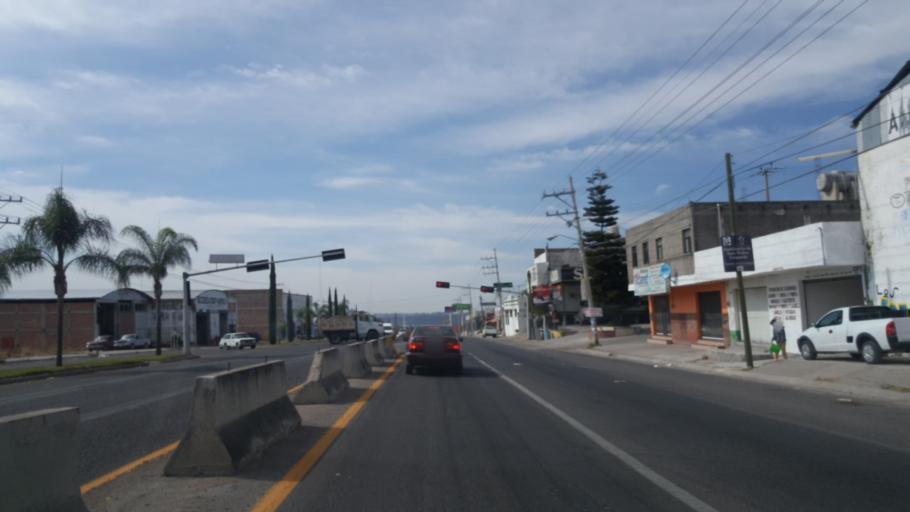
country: MX
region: Jalisco
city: San Juan de los Lagos
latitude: 21.2624
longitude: -102.3169
